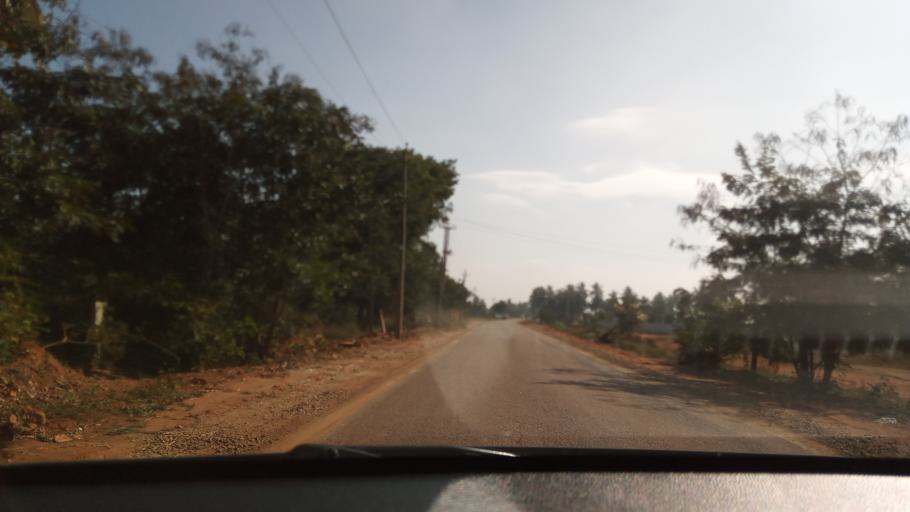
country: IN
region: Karnataka
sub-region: Bangalore Rural
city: Vijayapura
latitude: 13.2892
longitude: 77.7788
